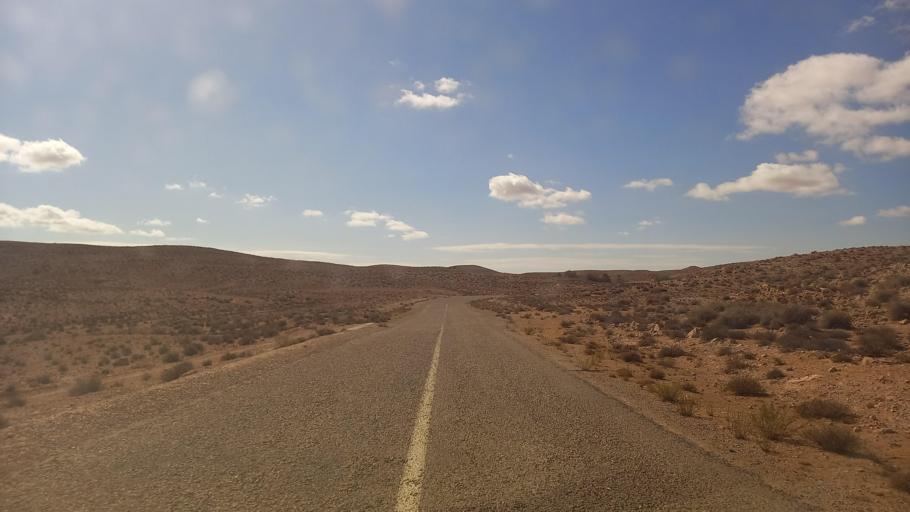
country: TN
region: Tataouine
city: Tataouine
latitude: 32.8785
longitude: 10.2400
